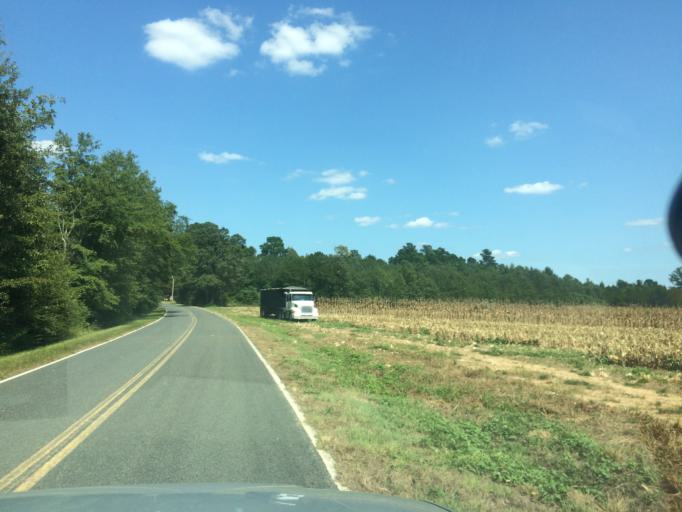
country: US
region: South Carolina
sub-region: Barnwell County
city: Williston
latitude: 33.6251
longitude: -81.4496
